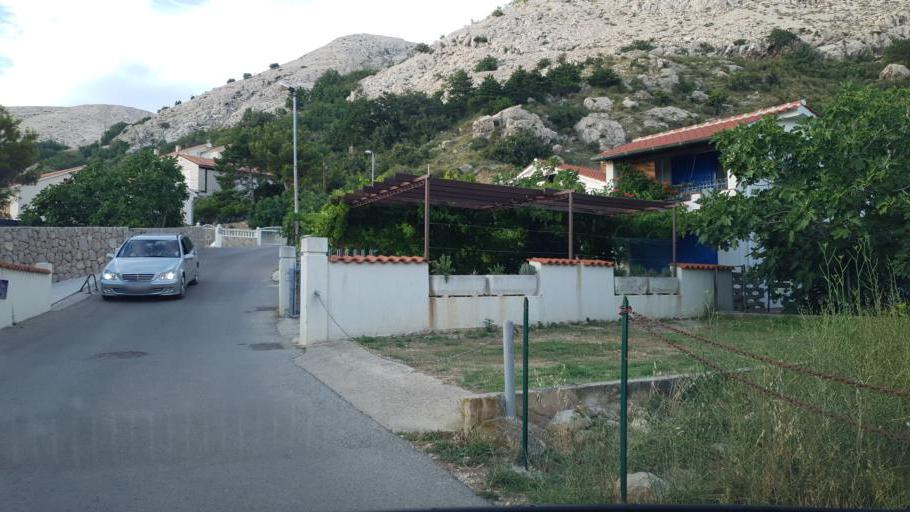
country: HR
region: Primorsko-Goranska
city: Punat
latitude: 44.9558
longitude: 14.6899
